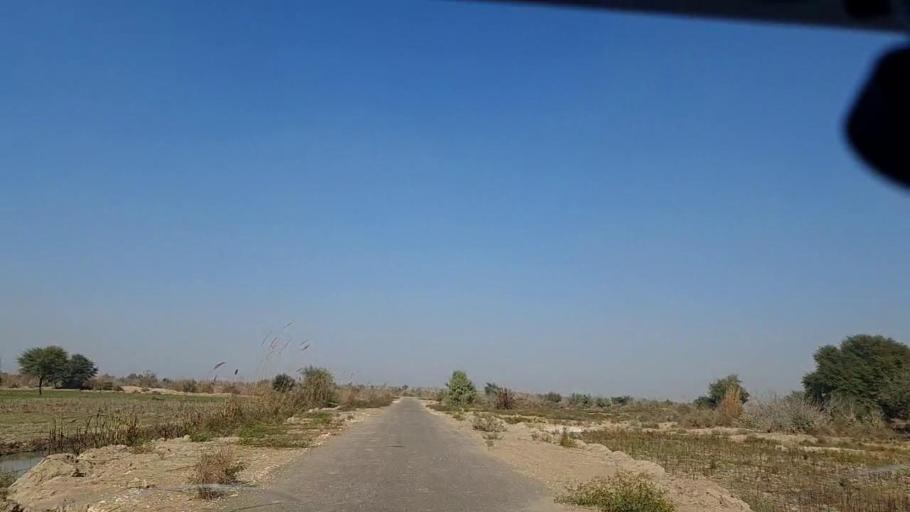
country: PK
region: Sindh
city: Khanpur
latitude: 27.5737
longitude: 69.3798
